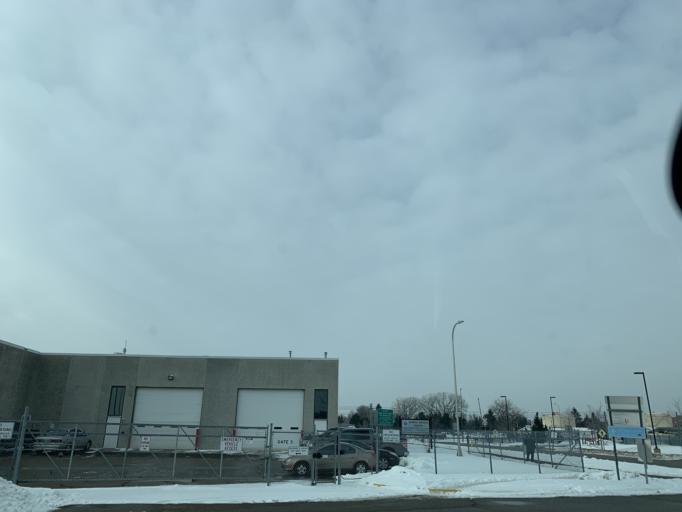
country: US
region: Minnesota
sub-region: Dakota County
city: Mendota Heights
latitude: 44.8921
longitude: -93.1969
